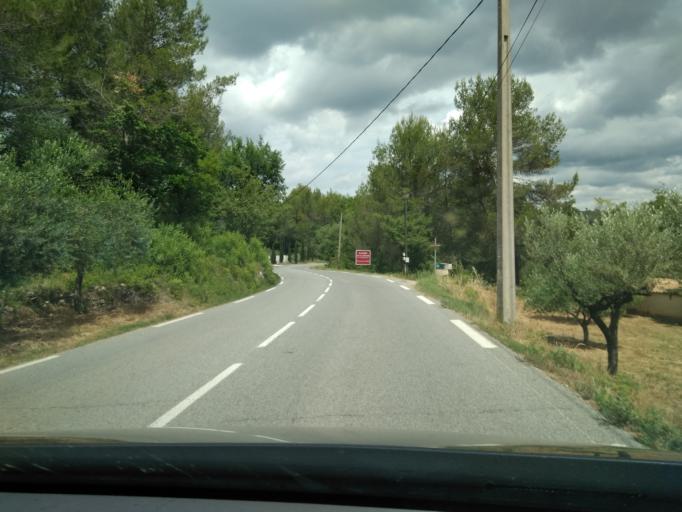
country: FR
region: Provence-Alpes-Cote d'Azur
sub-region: Departement du Var
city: Le Val
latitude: 43.4478
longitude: 6.0950
